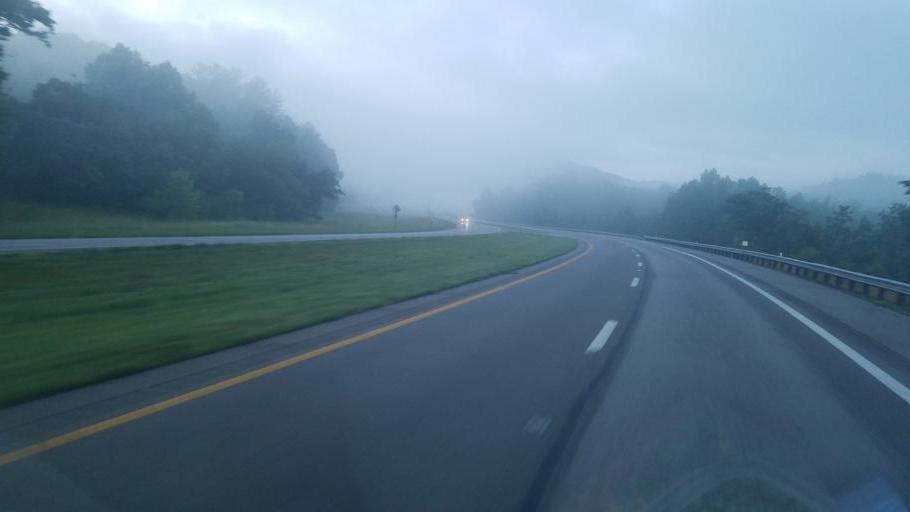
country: US
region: Ohio
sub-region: Jackson County
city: Jackson
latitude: 39.1675
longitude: -82.7428
